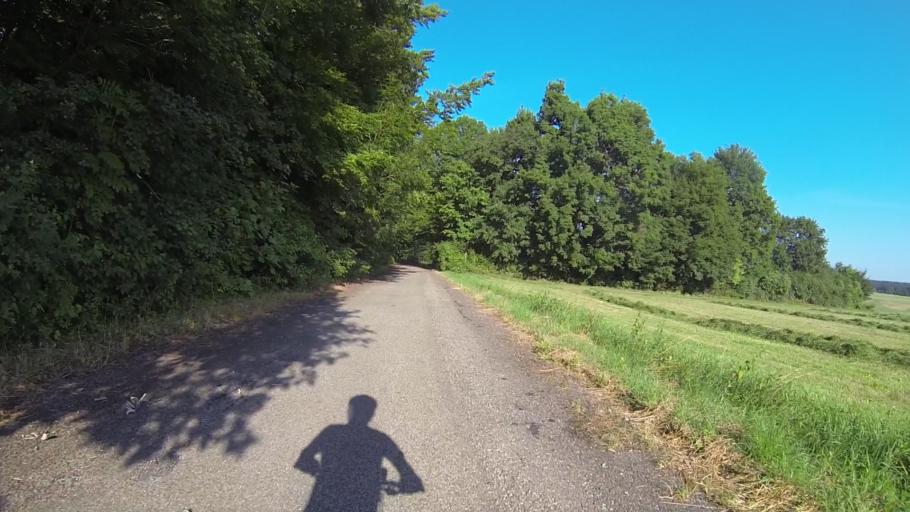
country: DE
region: Baden-Wuerttemberg
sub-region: Regierungsbezirk Stuttgart
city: Heidenheim an der Brenz
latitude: 48.6980
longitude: 10.1312
